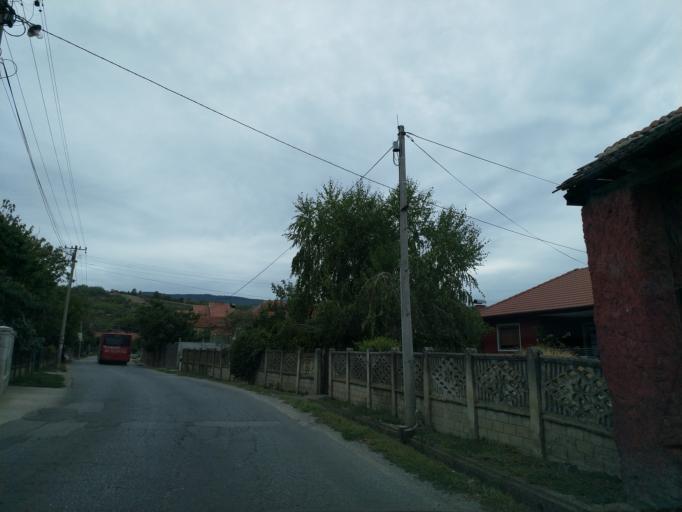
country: RS
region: Central Serbia
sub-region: Pomoravski Okrug
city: Paracin
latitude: 43.8356
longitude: 21.3249
